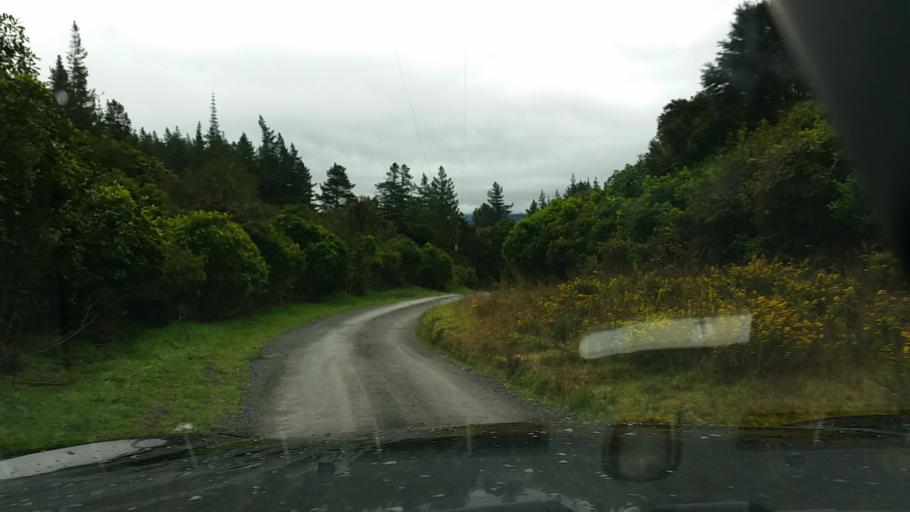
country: NZ
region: Marlborough
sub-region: Marlborough District
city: Picton
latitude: -41.2900
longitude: 174.0400
